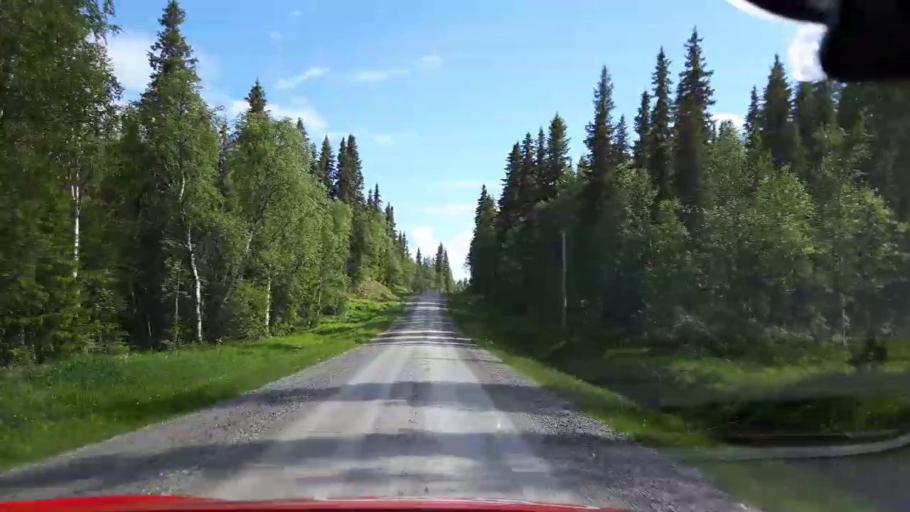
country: SE
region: Jaemtland
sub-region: Krokoms Kommun
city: Valla
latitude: 63.7955
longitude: 14.0465
